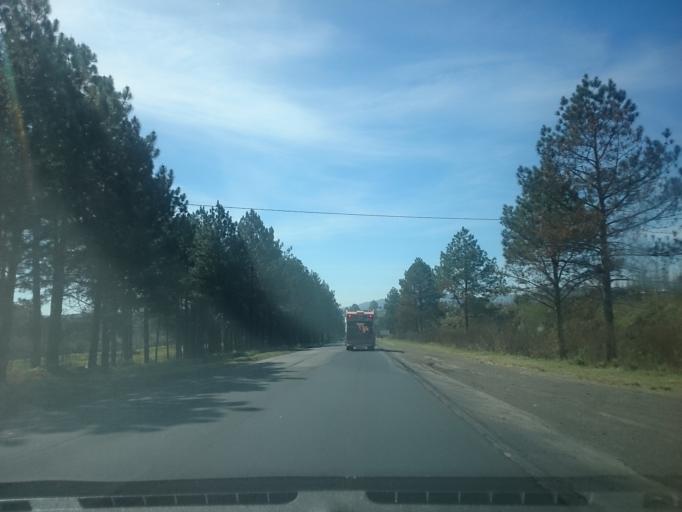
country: BR
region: Santa Catarina
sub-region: Lages
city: Lages
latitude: -27.7751
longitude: -50.2105
